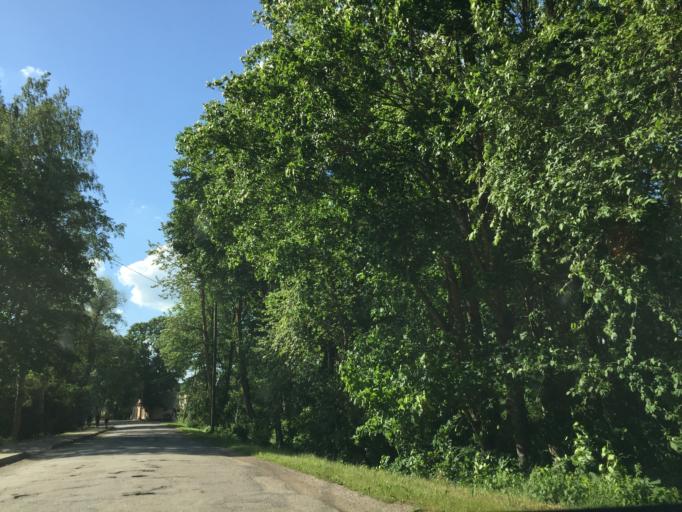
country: LV
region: Jaunpils
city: Jaunpils
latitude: 56.8743
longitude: 22.9986
